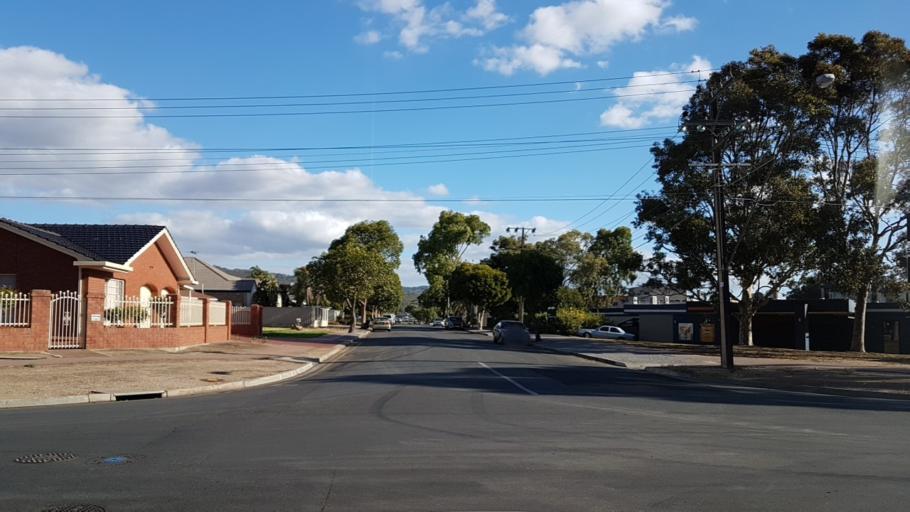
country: AU
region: South Australia
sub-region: Campbelltown
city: Athelstone
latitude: -34.8759
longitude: 138.6909
